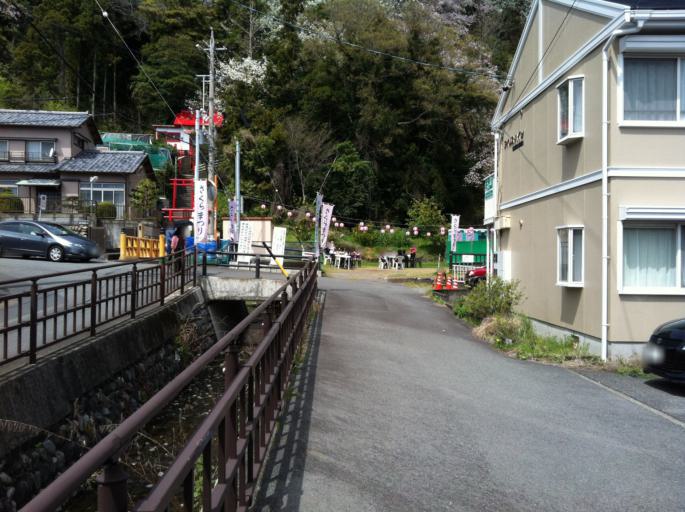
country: JP
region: Shizuoka
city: Fuji
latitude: 35.1206
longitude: 138.6060
